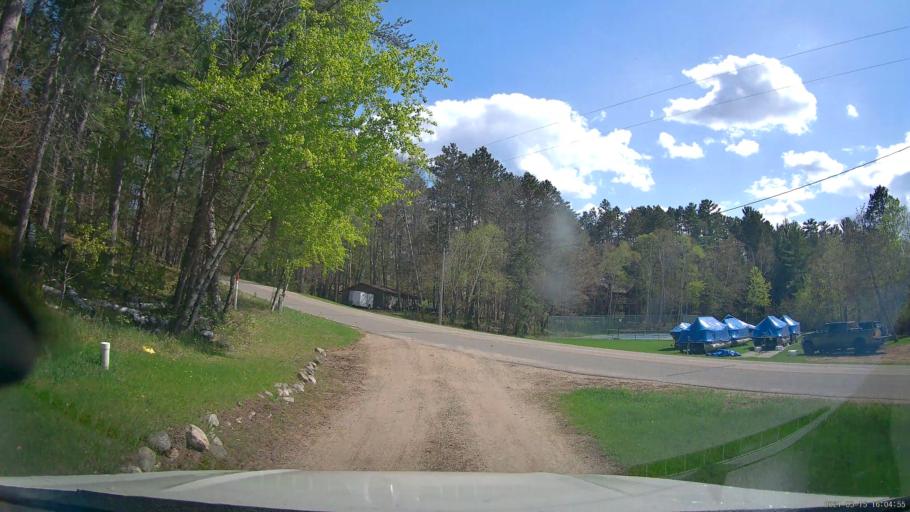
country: US
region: Minnesota
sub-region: Hubbard County
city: Park Rapids
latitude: 46.9861
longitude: -94.9503
